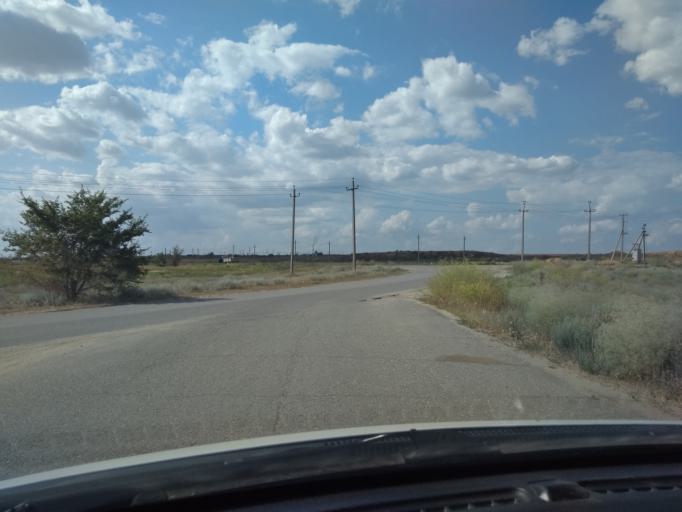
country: RU
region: Volgograd
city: Vodstroy
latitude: 48.8047
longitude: 44.5290
